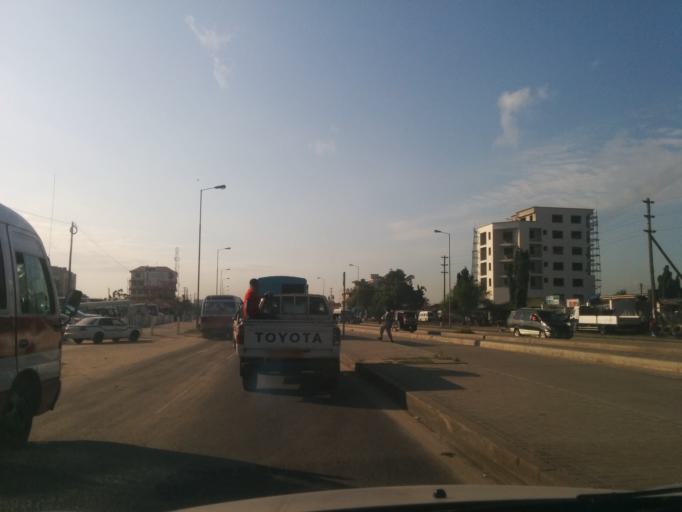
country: TZ
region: Dar es Salaam
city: Magomeni
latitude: -6.8030
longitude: 39.2459
